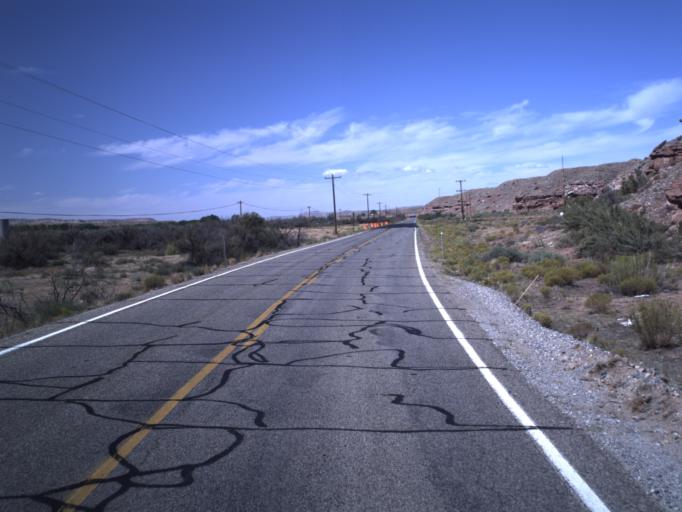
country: US
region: Colorado
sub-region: Montezuma County
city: Towaoc
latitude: 37.2200
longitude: -109.1973
